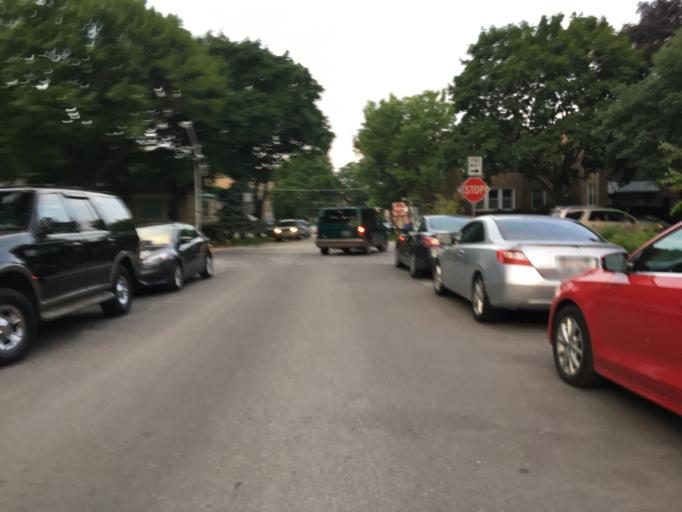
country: US
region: Illinois
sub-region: Cook County
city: Lincolnwood
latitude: 41.9721
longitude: -87.7017
